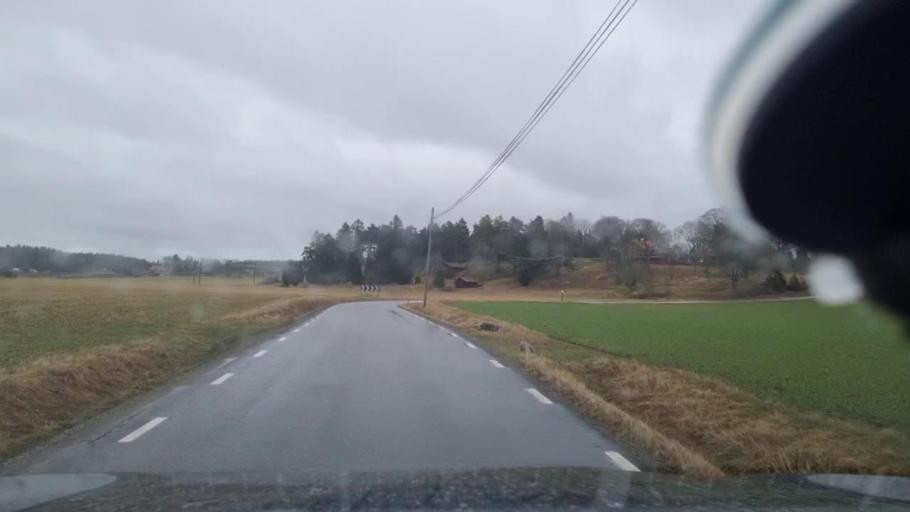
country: SE
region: Stockholm
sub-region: Vallentuna Kommun
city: Vallentuna
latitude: 59.5179
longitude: 18.0152
